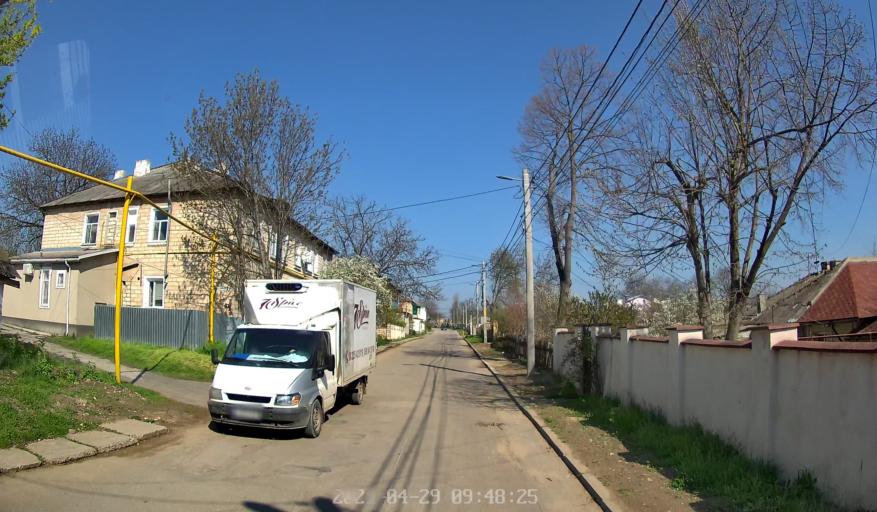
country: MD
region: Chisinau
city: Cricova
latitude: 47.1399
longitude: 28.8625
